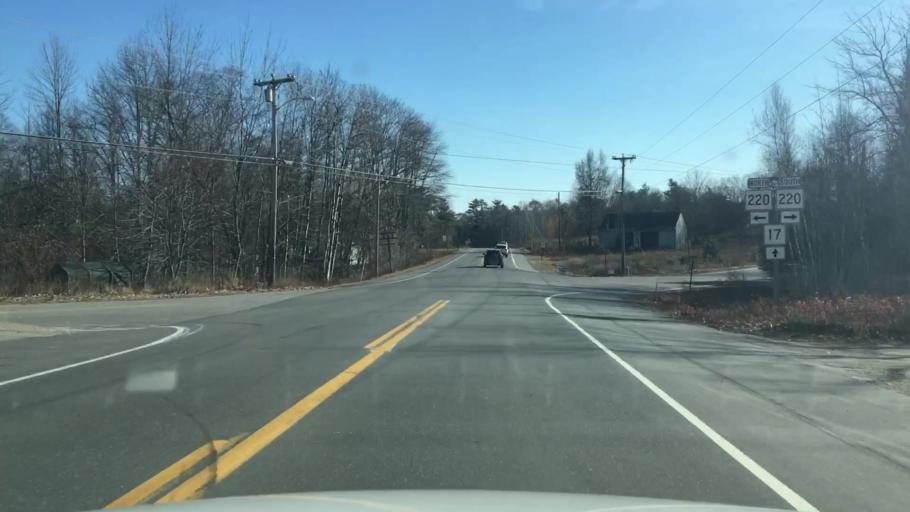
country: US
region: Maine
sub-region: Knox County
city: Washington
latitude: 44.2430
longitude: -69.3818
